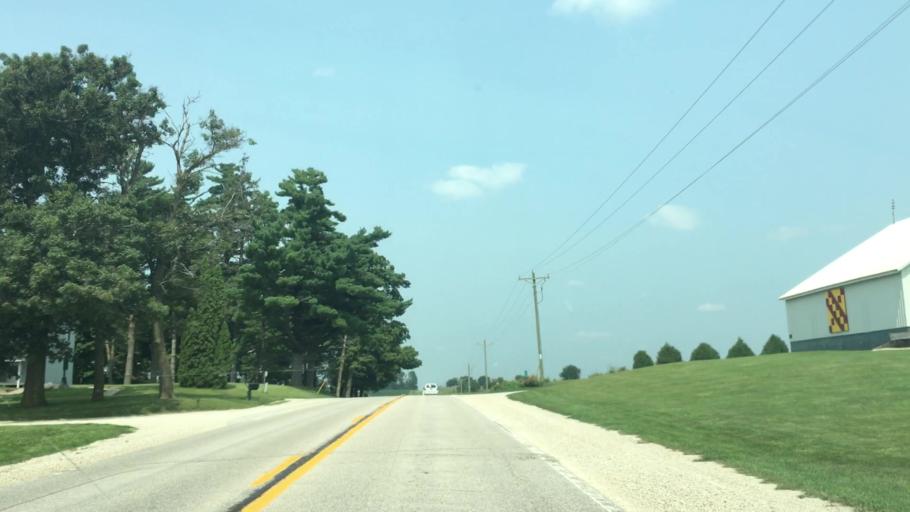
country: US
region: Iowa
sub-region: Benton County
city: Urbana
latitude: 42.3286
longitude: -91.8896
